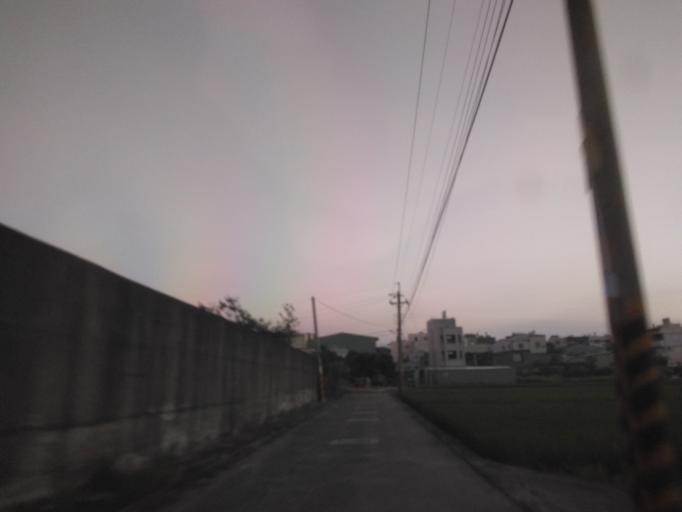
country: TW
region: Taiwan
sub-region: Changhua
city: Chang-hua
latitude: 24.0840
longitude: 120.5984
